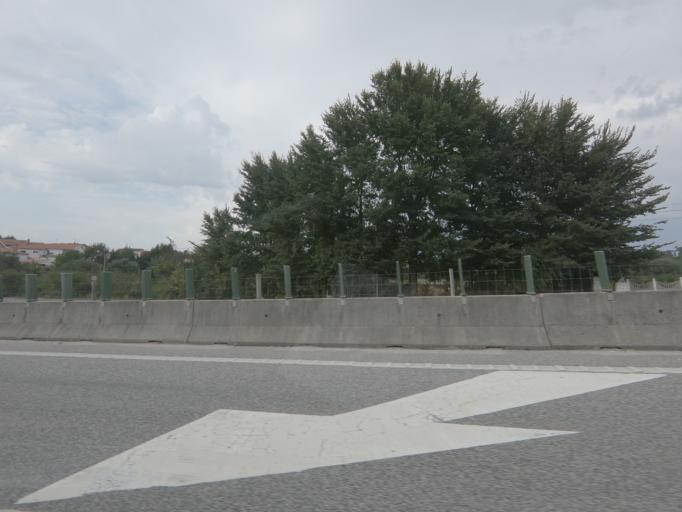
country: PT
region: Viseu
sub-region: Santa Comba Dao
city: Santa Comba Dao
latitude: 40.3858
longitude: -8.1205
